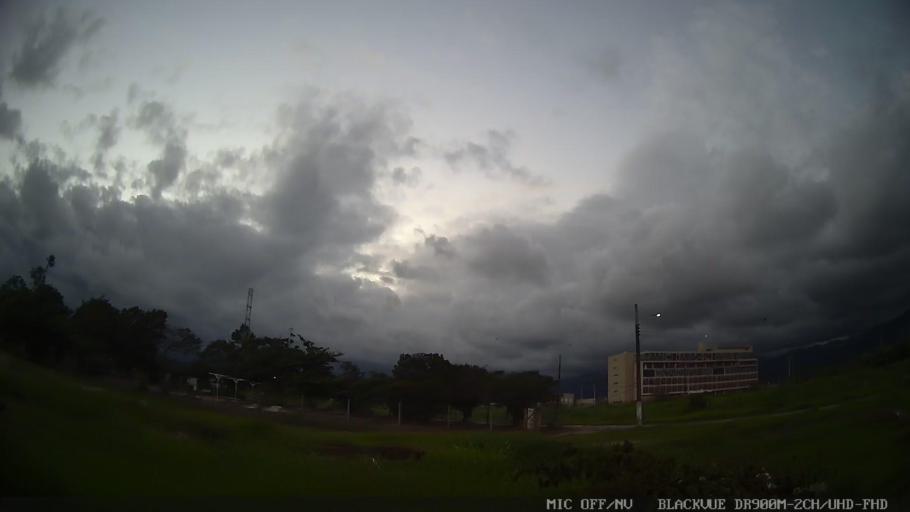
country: BR
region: Sao Paulo
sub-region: Caraguatatuba
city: Caraguatatuba
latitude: -23.6597
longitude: -45.4379
